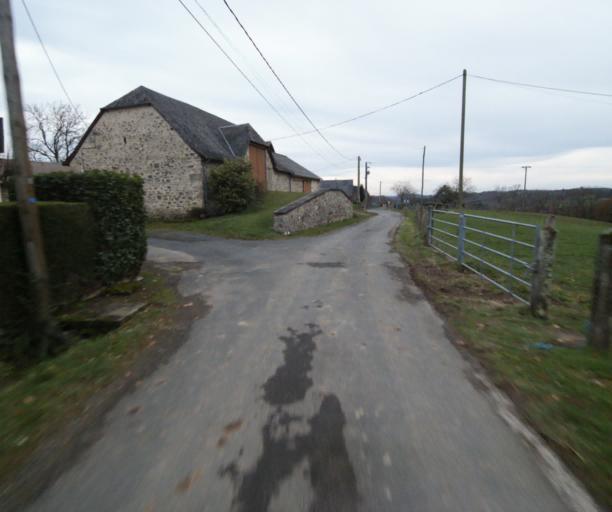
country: FR
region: Limousin
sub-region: Departement de la Correze
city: Saint-Mexant
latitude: 45.2495
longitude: 1.6581
